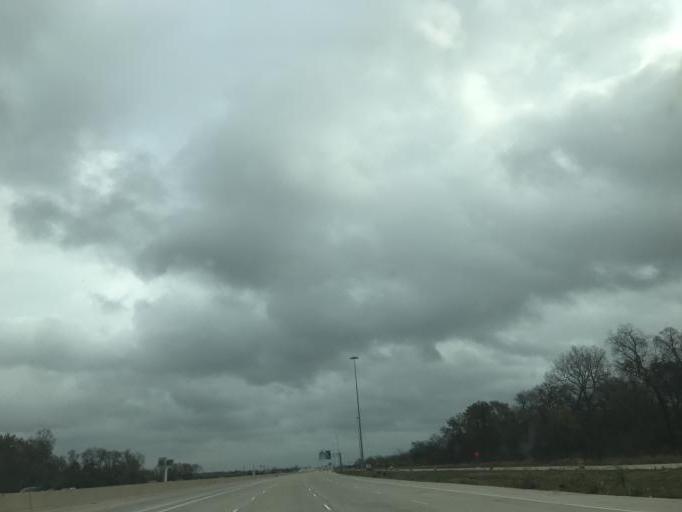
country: US
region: Texas
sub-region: Fort Bend County
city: Richmond
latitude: 29.5530
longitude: -95.7305
